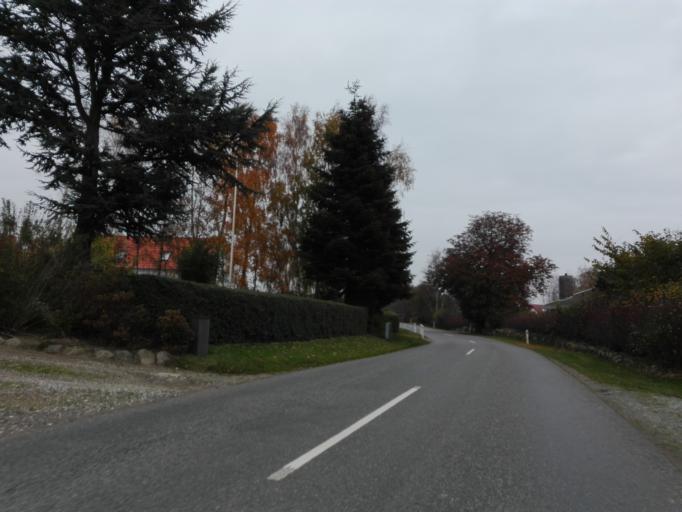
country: DK
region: Central Jutland
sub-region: Arhus Kommune
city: Beder
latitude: 56.0458
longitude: 10.2405
